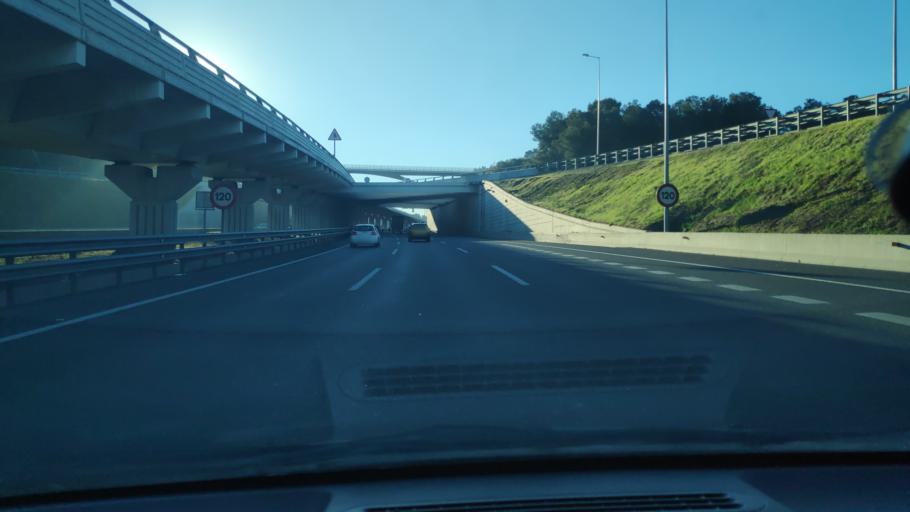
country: ES
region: Catalonia
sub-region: Provincia de Barcelona
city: Ripollet
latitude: 41.4800
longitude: 2.1606
